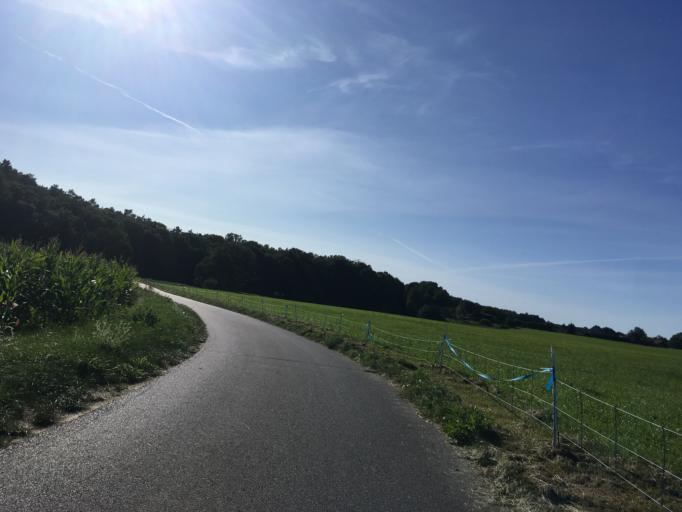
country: PL
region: Lubusz
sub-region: Powiat zarski
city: Przewoz
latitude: 51.4801
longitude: 14.9146
